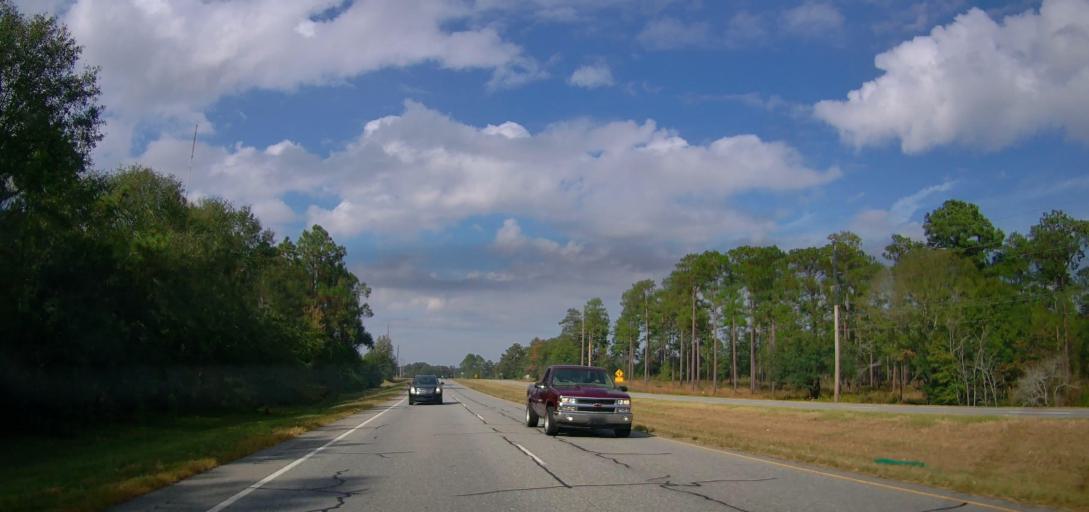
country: US
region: Georgia
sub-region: Mitchell County
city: Pelham
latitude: 31.1679
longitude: -84.1458
